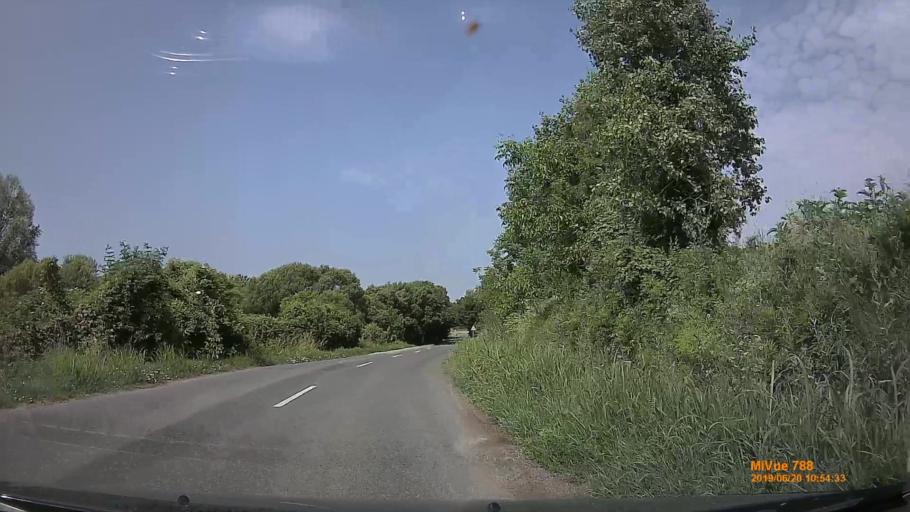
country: HU
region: Baranya
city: Mecseknadasd
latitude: 46.1533
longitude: 18.5635
